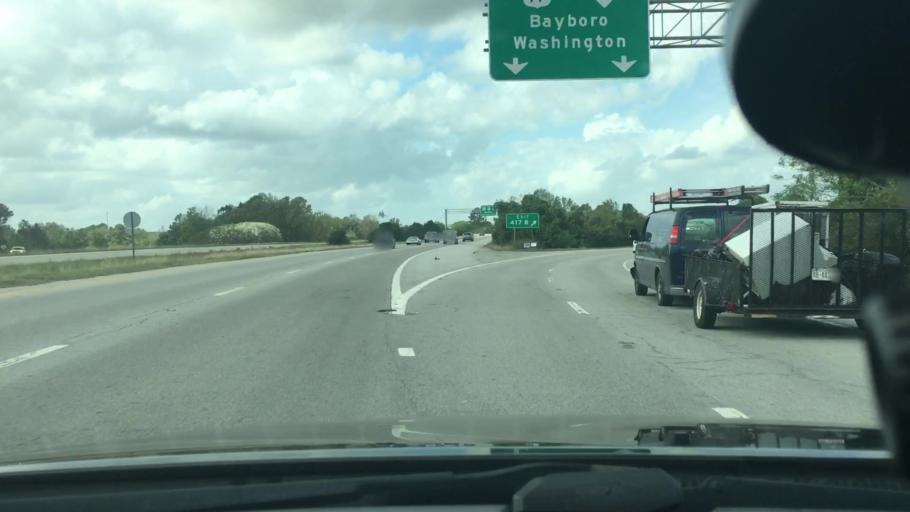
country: US
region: North Carolina
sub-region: Craven County
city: James City
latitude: 35.0892
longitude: -77.0352
